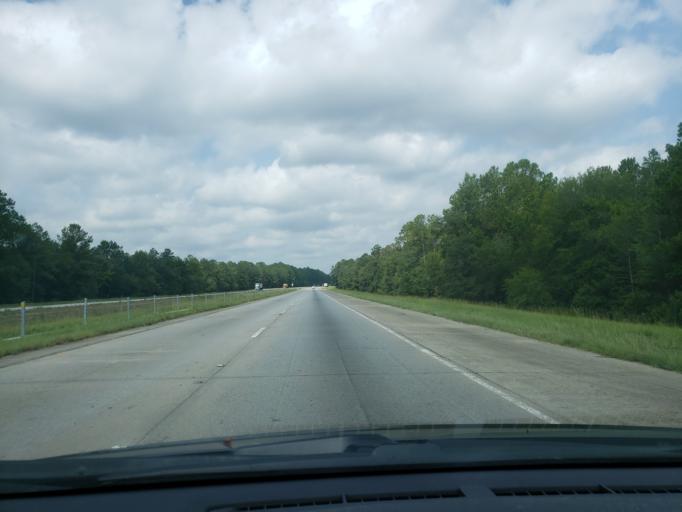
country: US
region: Georgia
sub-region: Emanuel County
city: Swainsboro
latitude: 32.4082
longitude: -82.3412
